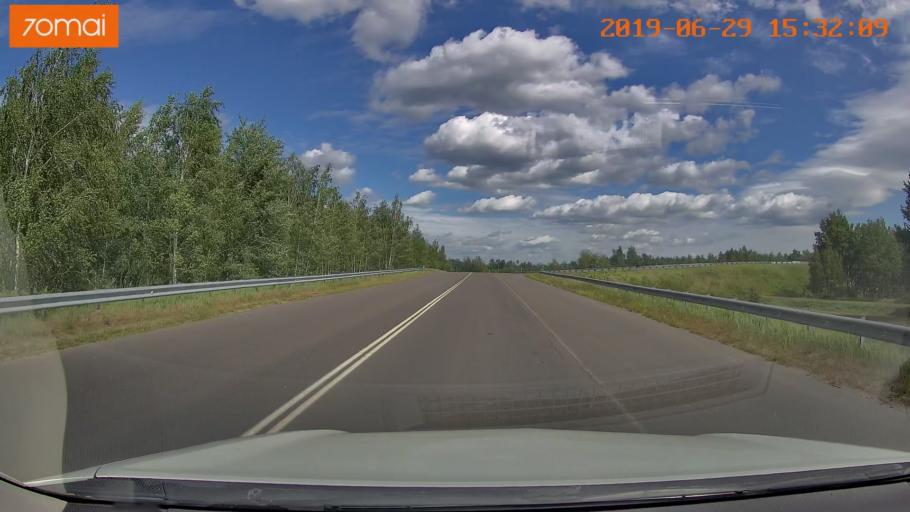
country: BY
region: Brest
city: Mikashevichy
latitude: 52.2104
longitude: 27.4146
